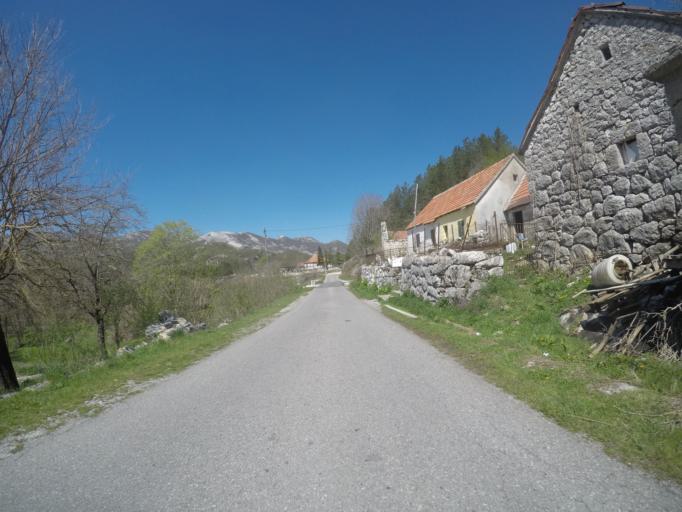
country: ME
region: Cetinje
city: Cetinje
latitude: 42.4636
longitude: 18.8625
